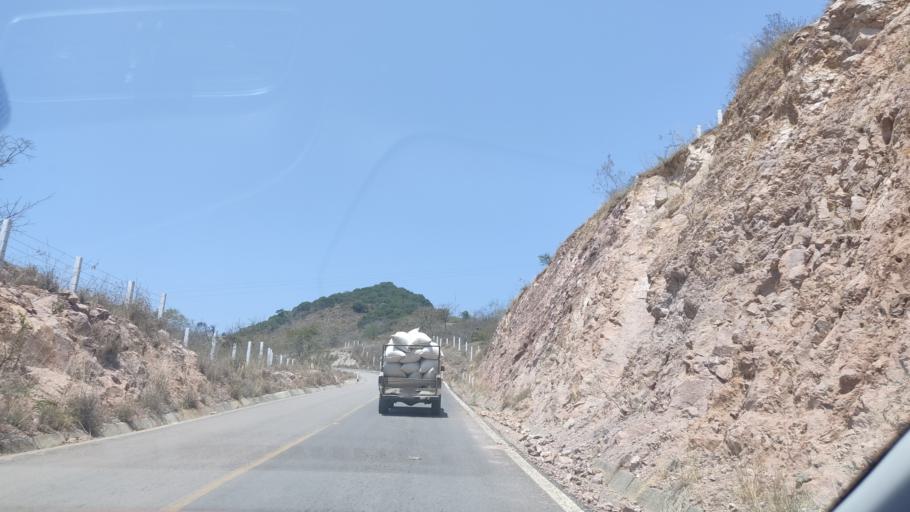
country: MX
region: Nayarit
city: Puga
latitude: 21.6191
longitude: -104.7159
